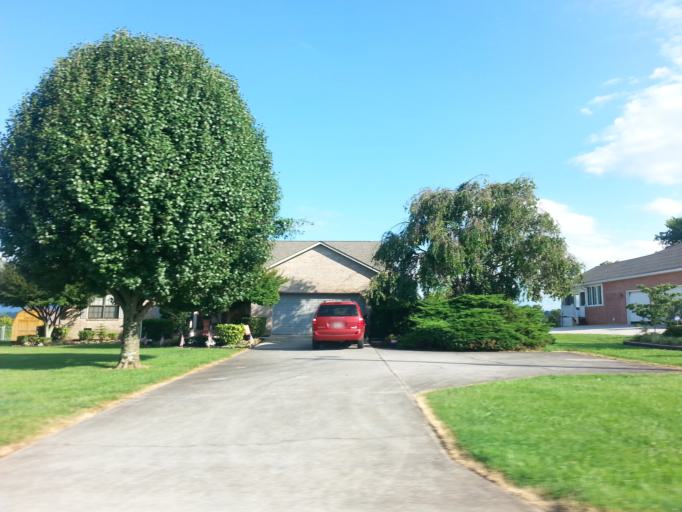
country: US
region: Tennessee
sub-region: Loudon County
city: Greenback
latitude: 35.6633
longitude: -84.0836
